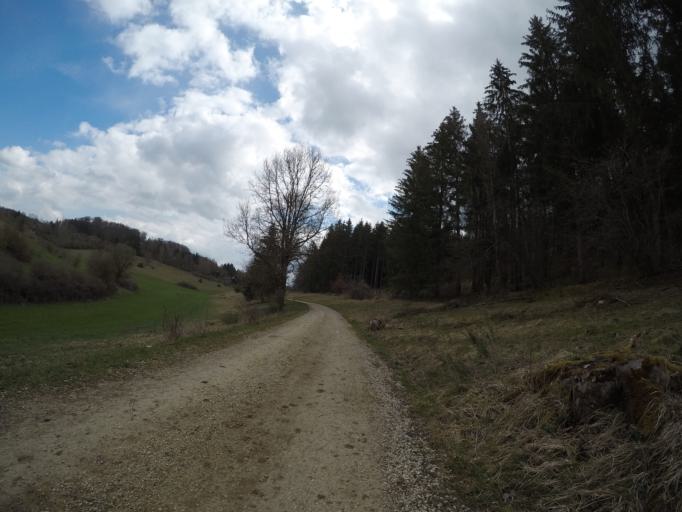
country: DE
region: Baden-Wuerttemberg
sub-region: Tuebingen Region
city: Merklingen
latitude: 48.5083
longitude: 9.7729
